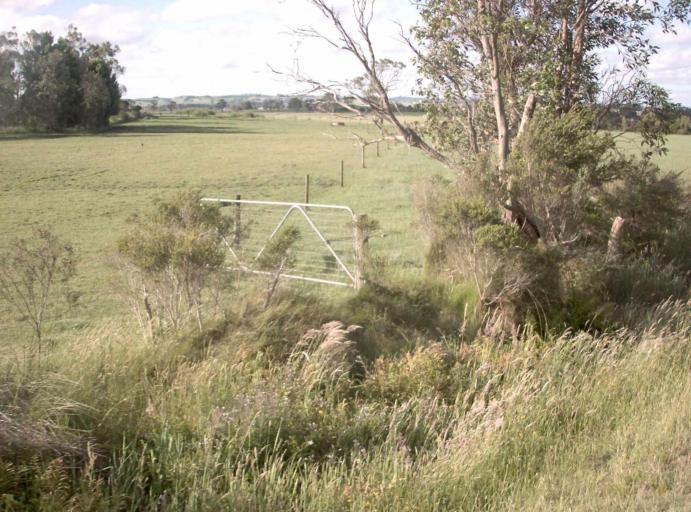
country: AU
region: Victoria
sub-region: Bass Coast
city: North Wonthaggi
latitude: -38.5471
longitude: 145.8508
